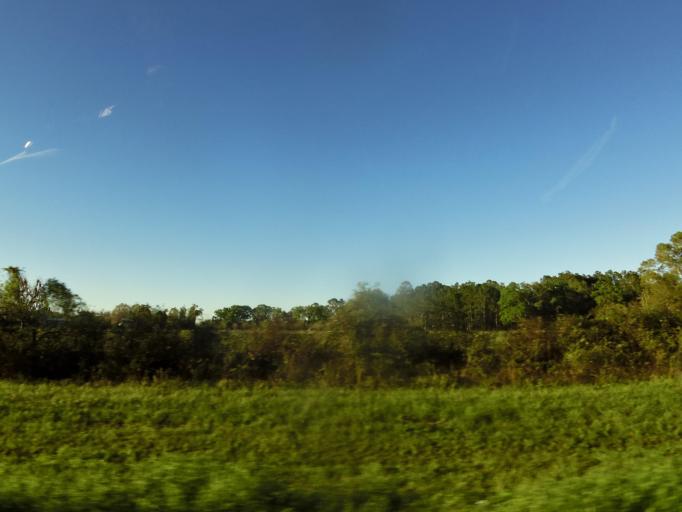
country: US
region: Florida
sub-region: Bradford County
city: Starke
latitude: 29.8646
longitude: -82.1243
